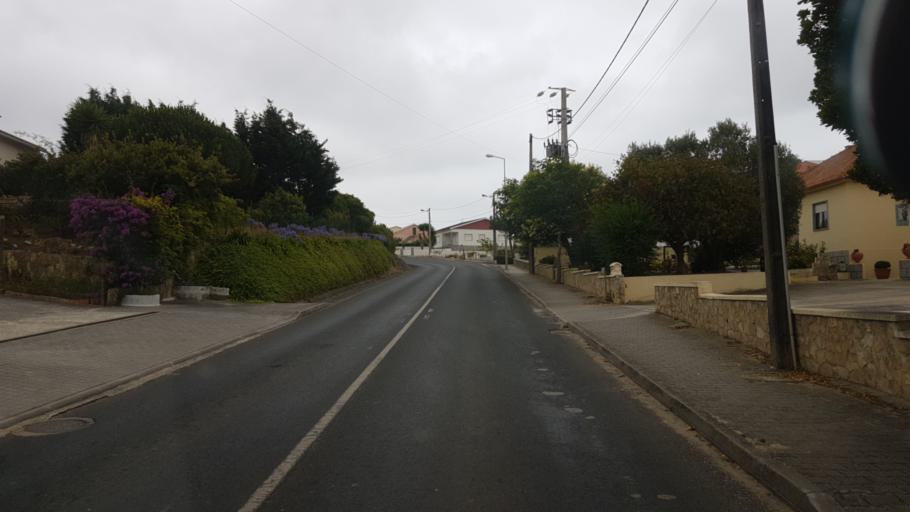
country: PT
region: Lisbon
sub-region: Lourinha
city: Lourinha
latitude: 39.2208
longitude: -9.3185
